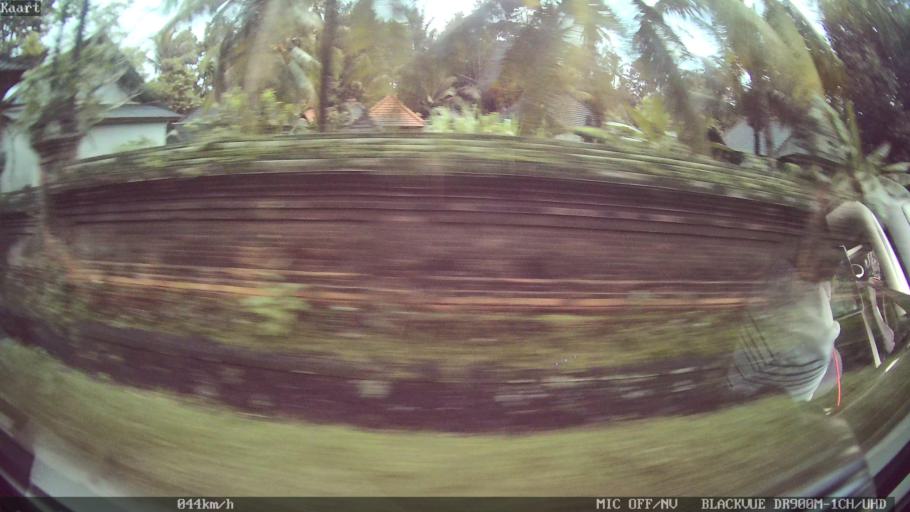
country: ID
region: Bali
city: Banjar Teguan
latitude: -8.4983
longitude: 115.2346
